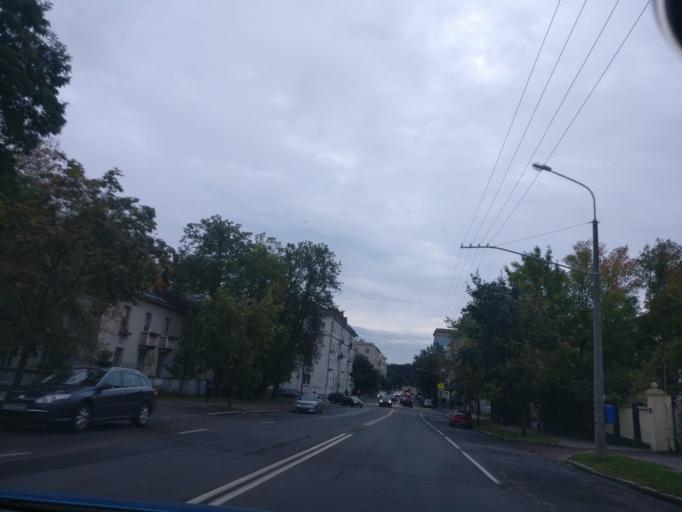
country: BY
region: Minsk
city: Minsk
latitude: 53.9263
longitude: 27.6067
